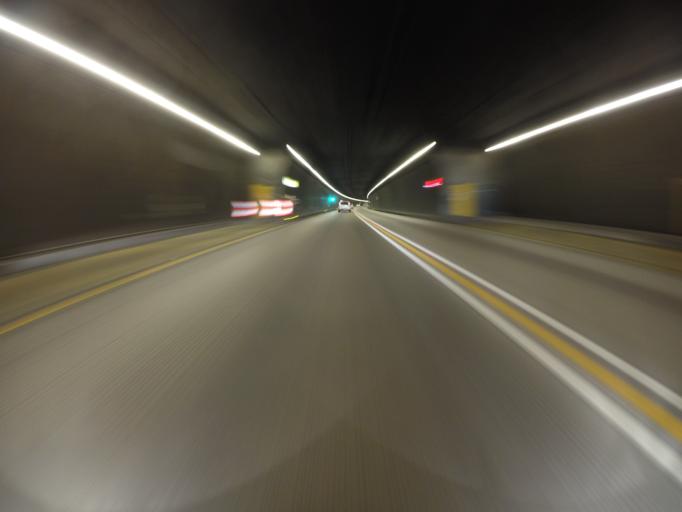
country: ZA
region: Western Cape
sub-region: Cape Winelands District Municipality
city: Paarl
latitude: -33.7343
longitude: 19.0718
